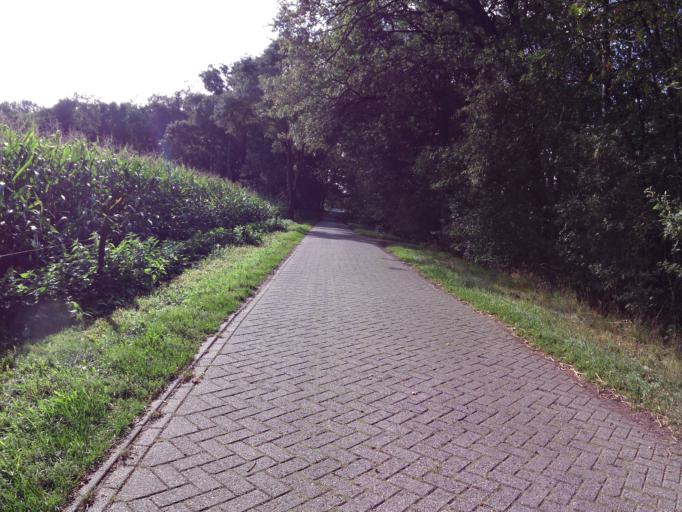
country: NL
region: Overijssel
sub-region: Gemeente Haaksbergen
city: Haaksbergen
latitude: 52.1527
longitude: 6.8172
